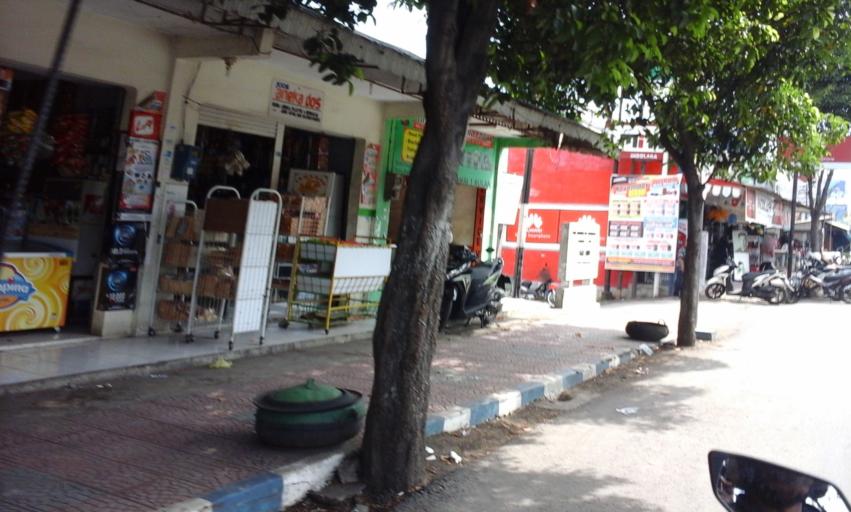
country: ID
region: East Java
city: Krajan
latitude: -8.2386
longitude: 114.3565
